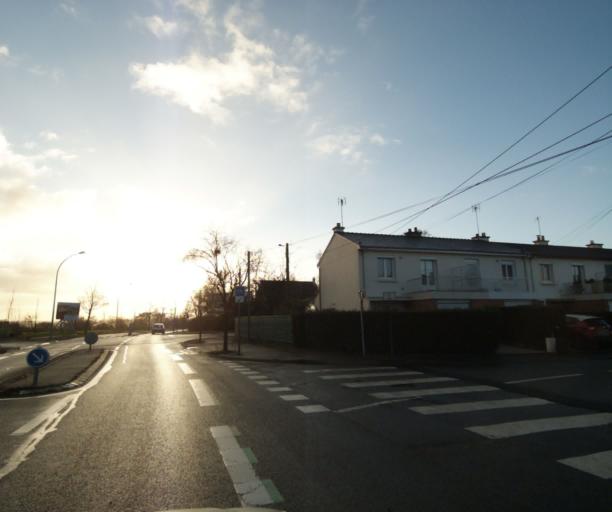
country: FR
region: Pays de la Loire
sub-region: Departement de la Sarthe
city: Sarge-les-le-Mans
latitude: 48.0092
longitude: 0.2265
